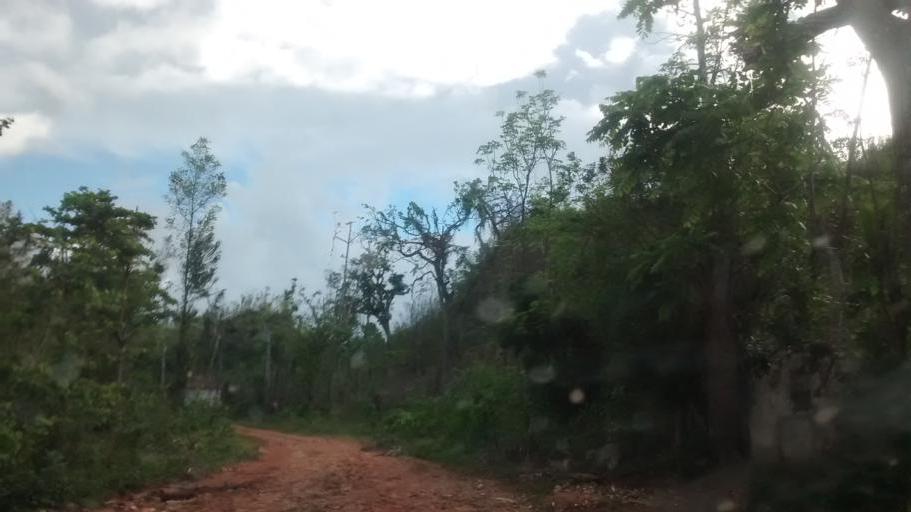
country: HT
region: Grandans
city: Corail
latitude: 18.5071
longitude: -73.7815
